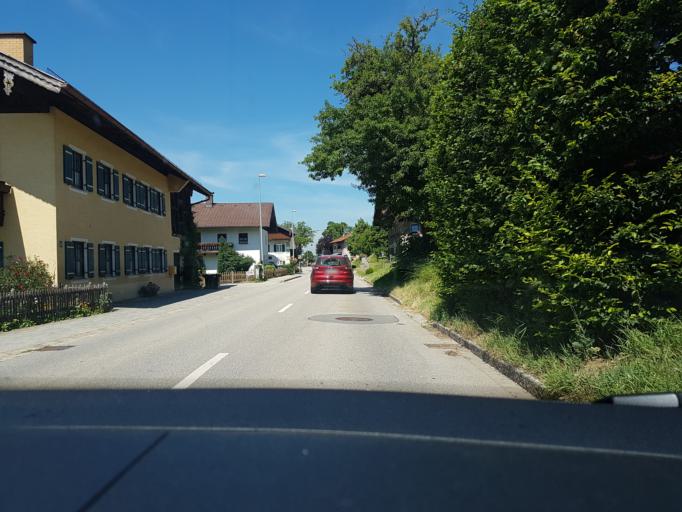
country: DE
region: Bavaria
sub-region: Upper Bavaria
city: Anger
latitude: 47.8380
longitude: 12.8940
